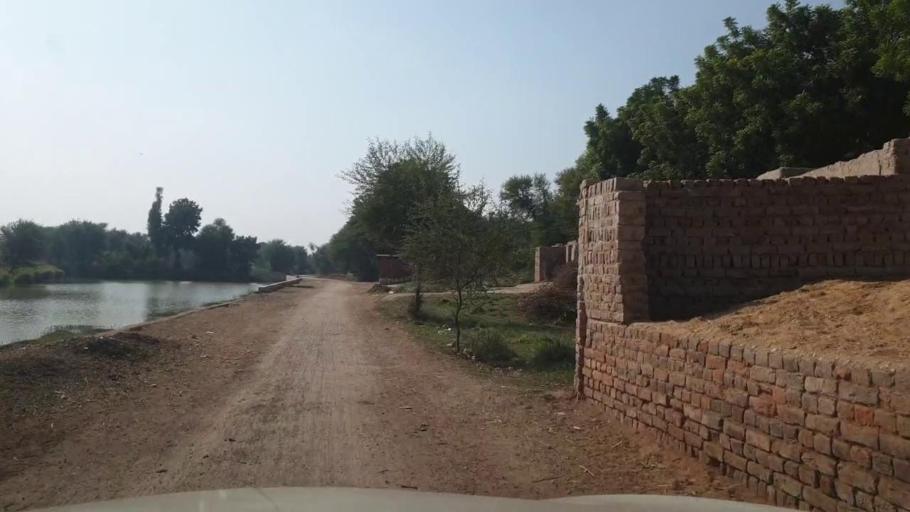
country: PK
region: Sindh
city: Bhan
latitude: 26.5164
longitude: 67.7778
